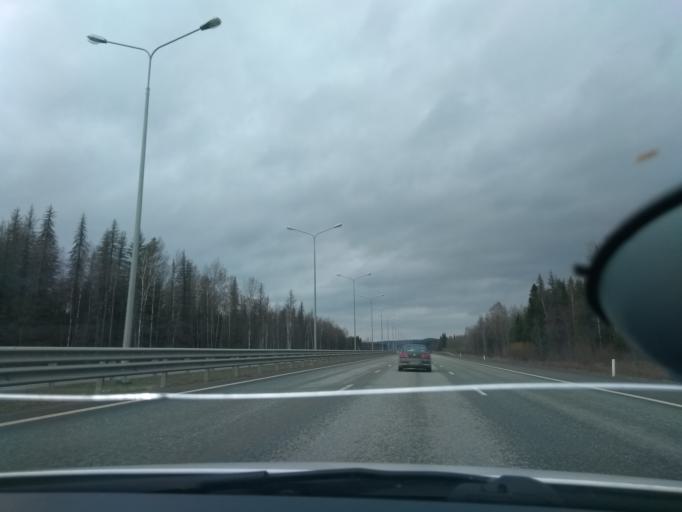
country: RU
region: Perm
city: Kukushtan
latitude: 57.6621
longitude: 56.4392
